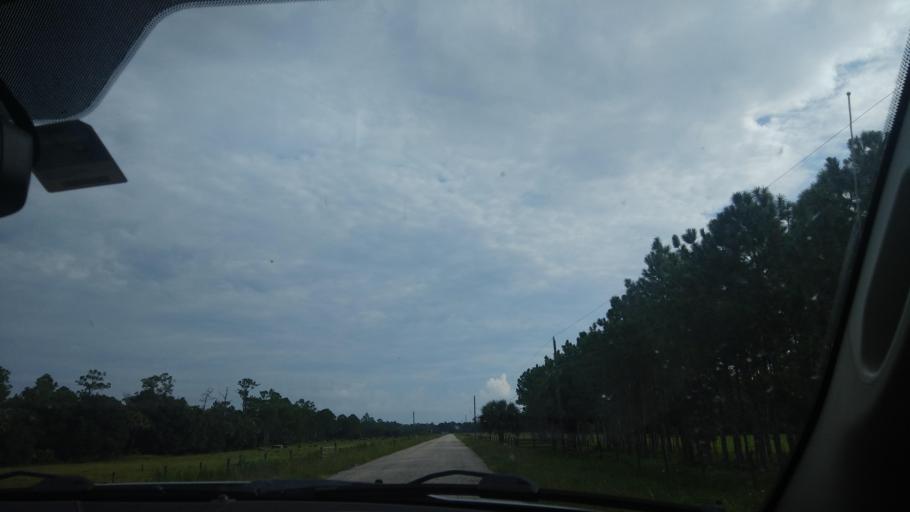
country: US
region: Florida
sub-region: Indian River County
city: Fellsmere
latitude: 27.6720
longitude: -80.8021
